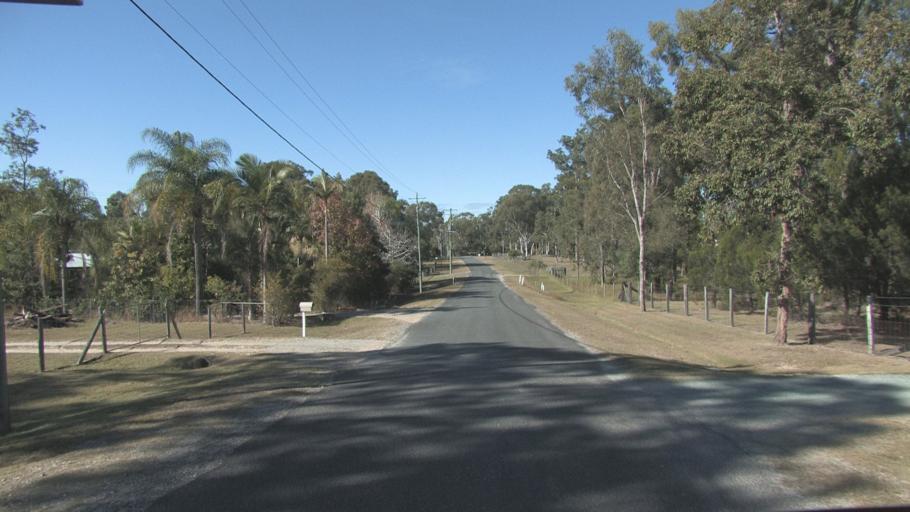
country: AU
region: Queensland
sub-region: Logan
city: Chambers Flat
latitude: -27.7781
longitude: 153.0771
